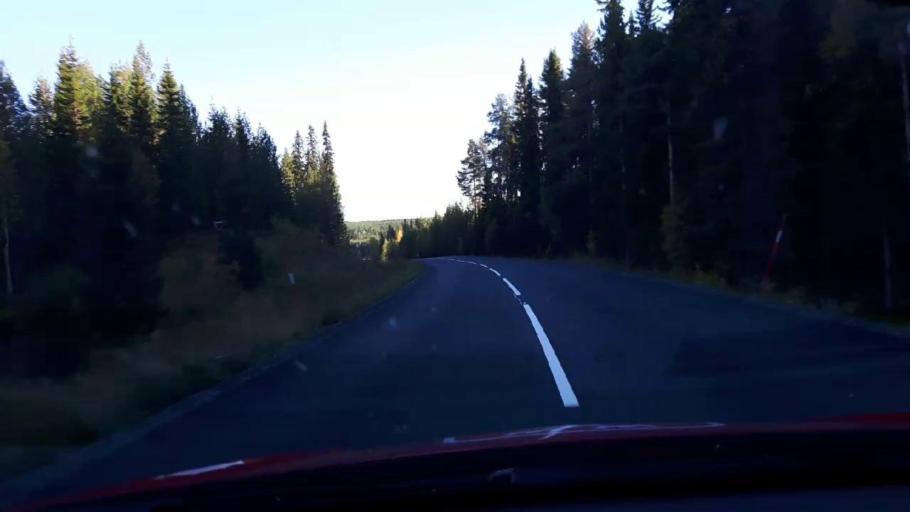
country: SE
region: Jaemtland
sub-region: OEstersunds Kommun
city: Lit
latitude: 63.5257
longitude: 14.8443
